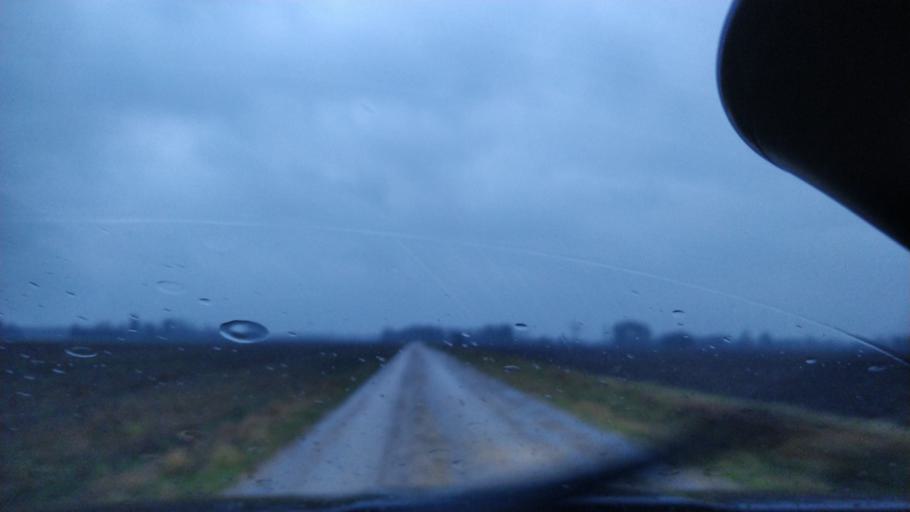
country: EE
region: Laeaene
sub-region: Lihula vald
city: Lihula
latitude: 58.8533
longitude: 23.9993
